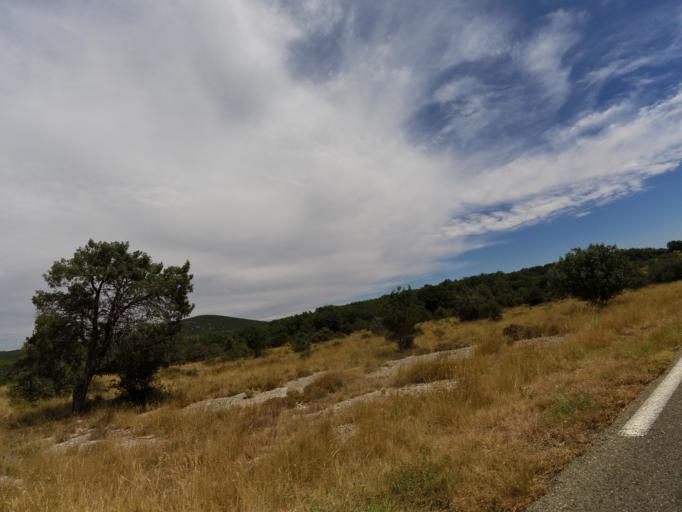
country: FR
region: Languedoc-Roussillon
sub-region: Departement du Gard
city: Saint-Hippolyte-du-Fort
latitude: 43.9504
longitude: 3.8832
